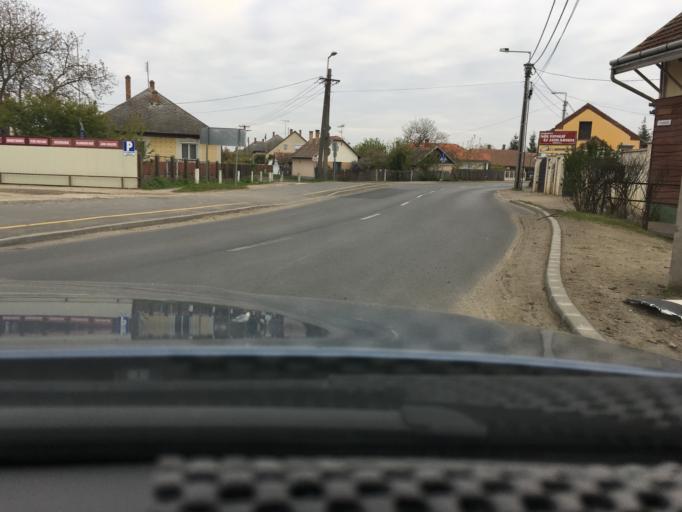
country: HU
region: Hajdu-Bihar
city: Hajdusamson
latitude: 47.6010
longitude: 21.7598
